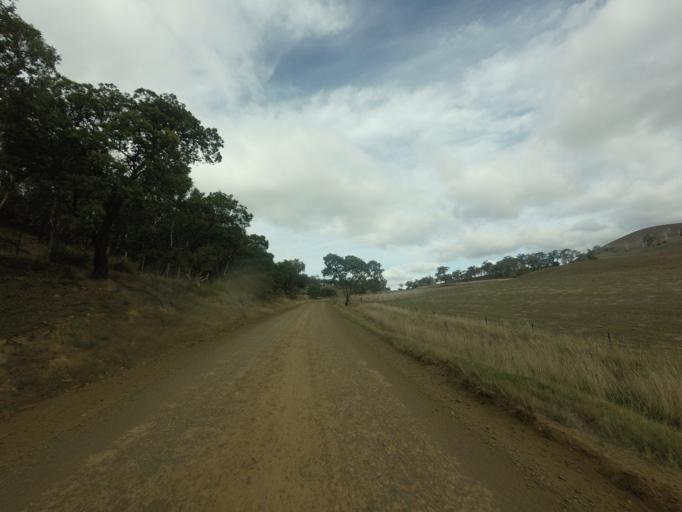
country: AU
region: Tasmania
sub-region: Brighton
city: Bridgewater
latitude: -42.4739
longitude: 147.2908
